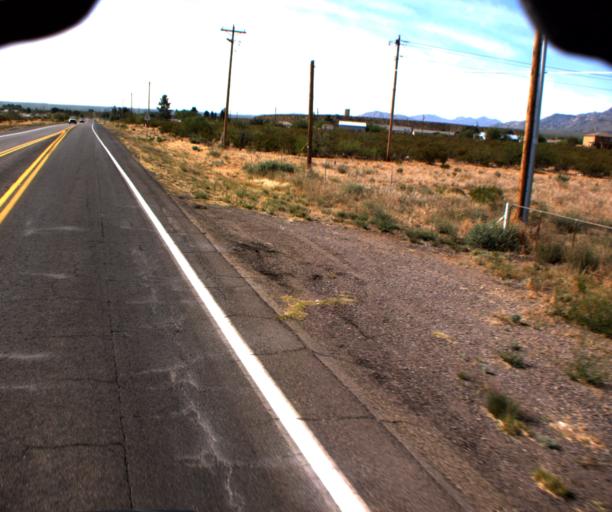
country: US
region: Arizona
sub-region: Graham County
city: Swift Trail Junction
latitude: 32.7287
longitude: -109.7138
